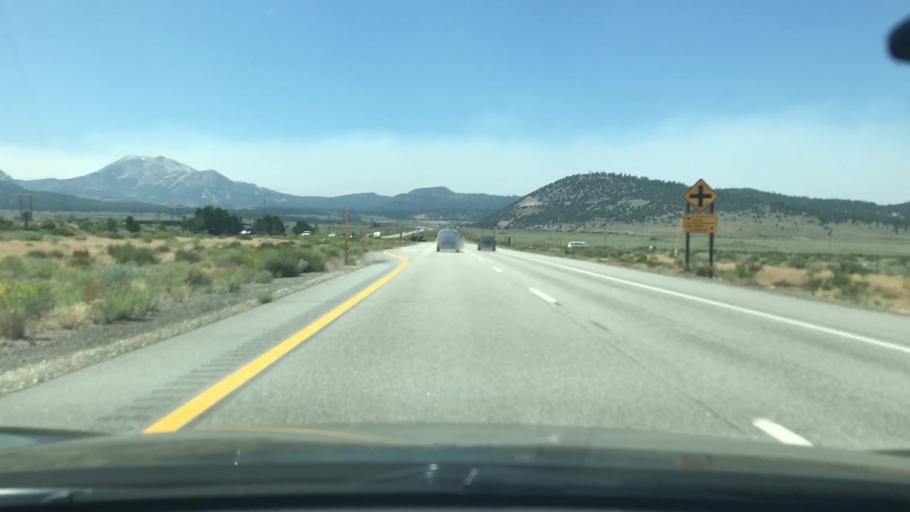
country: US
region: California
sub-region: Mono County
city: Mammoth Lakes
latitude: 37.6290
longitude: -118.8618
